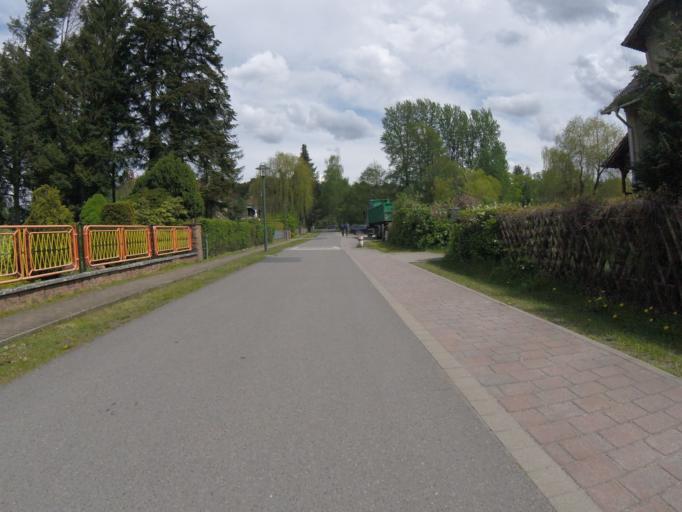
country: DE
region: Brandenburg
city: Schwerin
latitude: 52.1528
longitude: 13.6406
